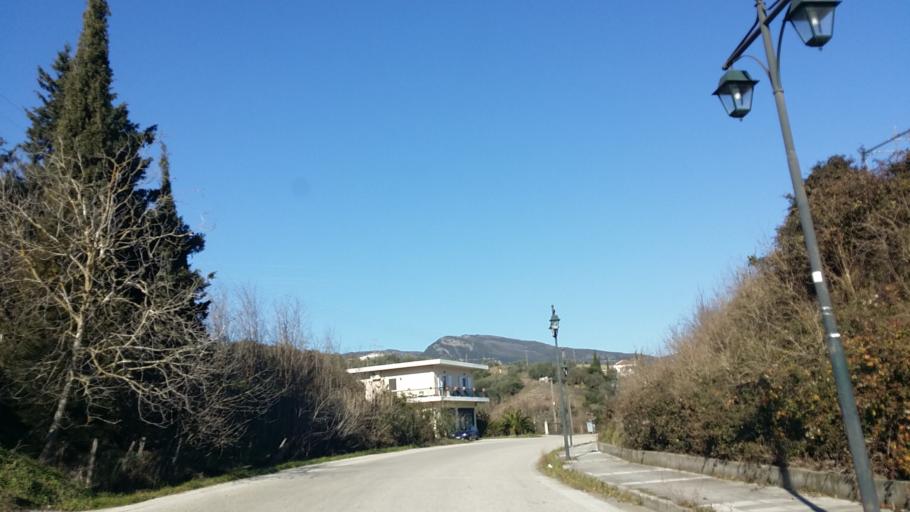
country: GR
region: West Greece
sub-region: Nomos Aitolias kai Akarnanias
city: Sardinia
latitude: 38.8554
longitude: 21.3360
